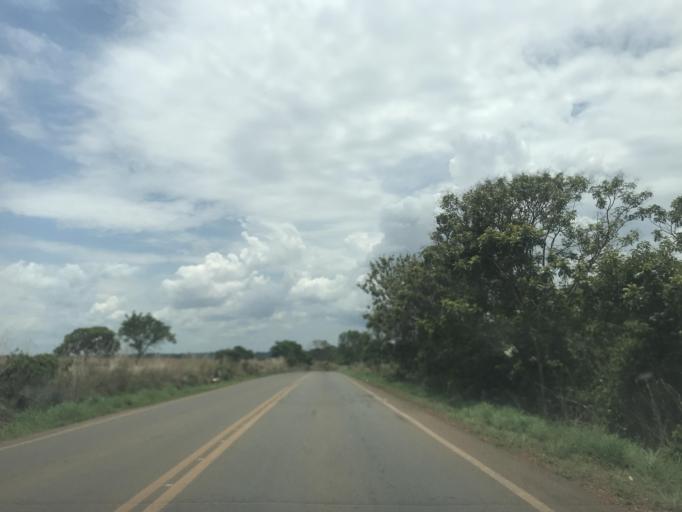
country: BR
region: Goias
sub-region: Vianopolis
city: Vianopolis
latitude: -16.7392
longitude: -48.4478
